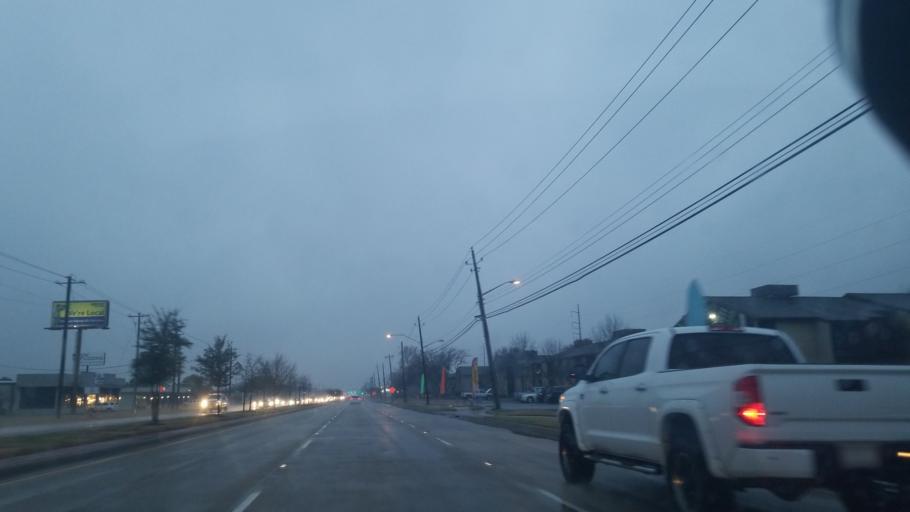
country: US
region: Texas
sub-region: Denton County
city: Denton
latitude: 33.2195
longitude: -97.0905
